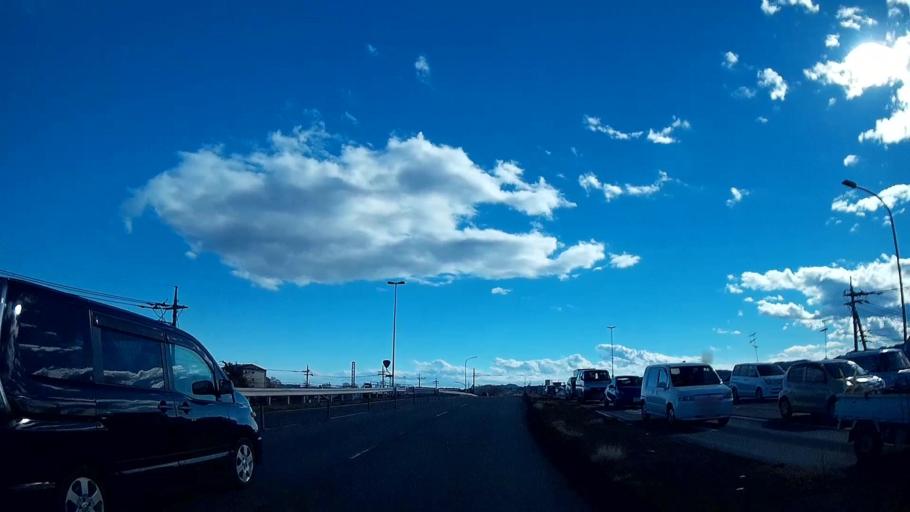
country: JP
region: Saitama
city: Yorii
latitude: 36.1259
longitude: 139.2016
